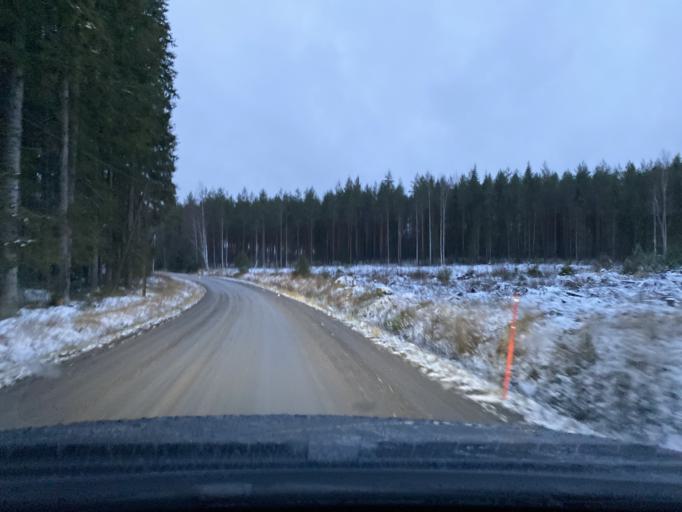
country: FI
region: Pirkanmaa
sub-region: Lounais-Pirkanmaa
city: Punkalaidun
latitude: 61.1506
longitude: 22.9480
